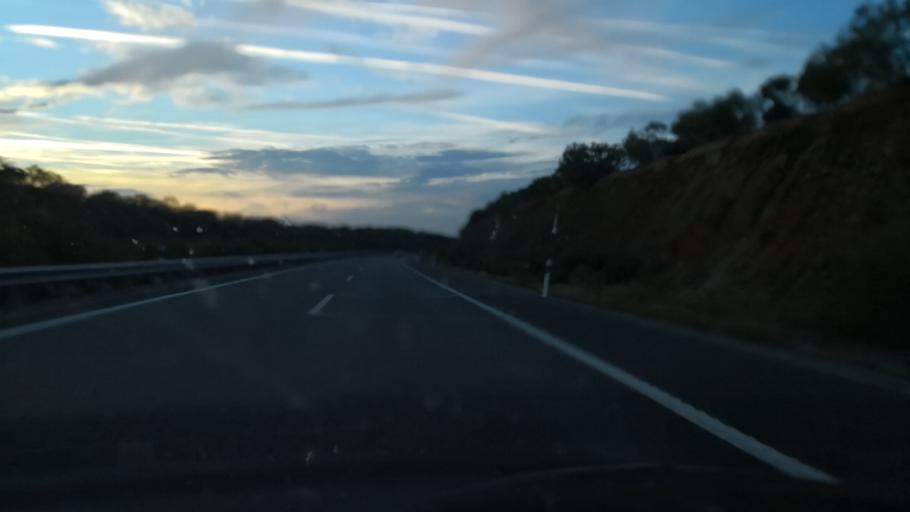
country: ES
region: Extremadura
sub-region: Provincia de Caceres
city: Aldea del Cano
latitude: 39.3380
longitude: -6.3373
